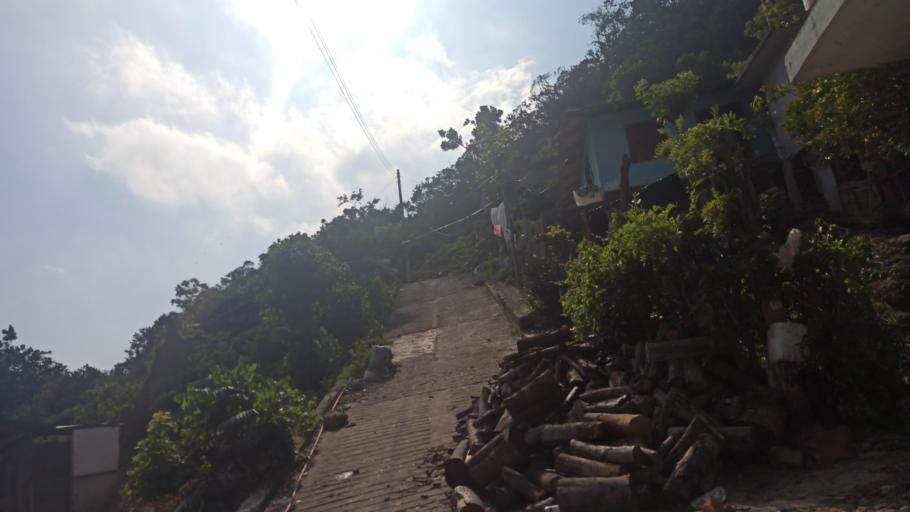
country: MX
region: Veracruz
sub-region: Cazones de Herrera
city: Rancho Nuevo
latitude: 20.6215
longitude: -97.2177
